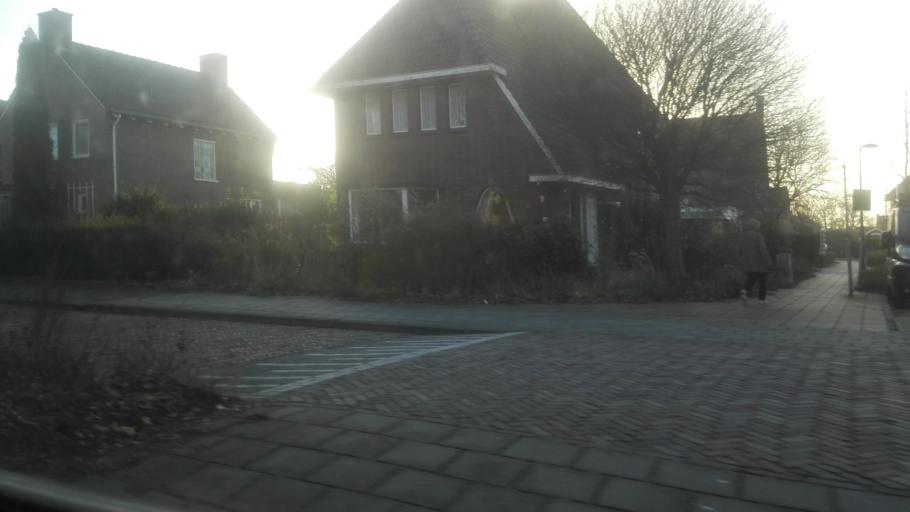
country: NL
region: Friesland
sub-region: Gemeente Heerenveen
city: Heerenveen
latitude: 52.9527
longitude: 5.9320
